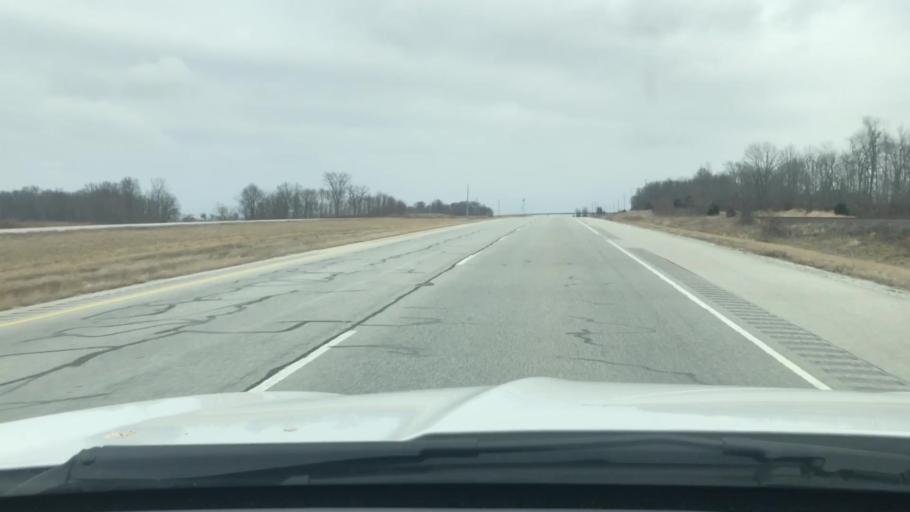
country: US
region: Indiana
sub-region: Cass County
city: Georgetown
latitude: 40.6538
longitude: -86.5517
